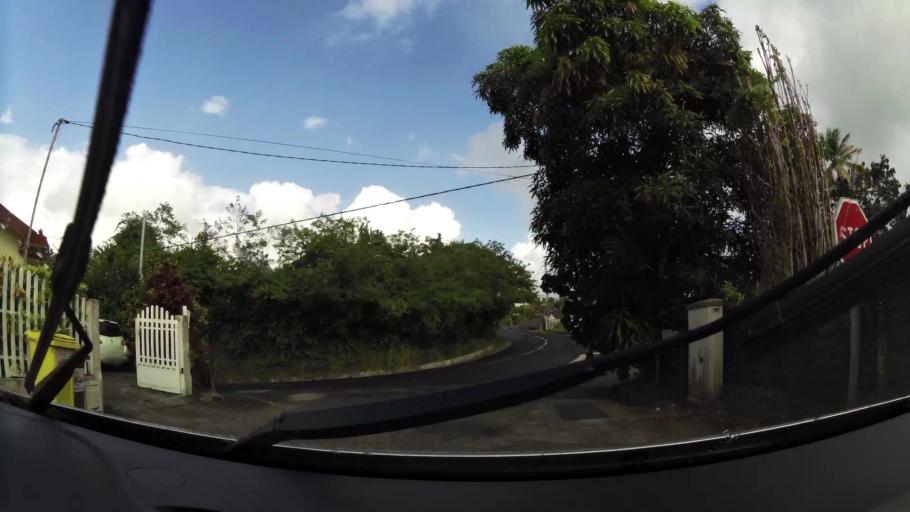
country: MQ
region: Martinique
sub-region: Martinique
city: Saint-Esprit
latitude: 14.5088
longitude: -60.9611
